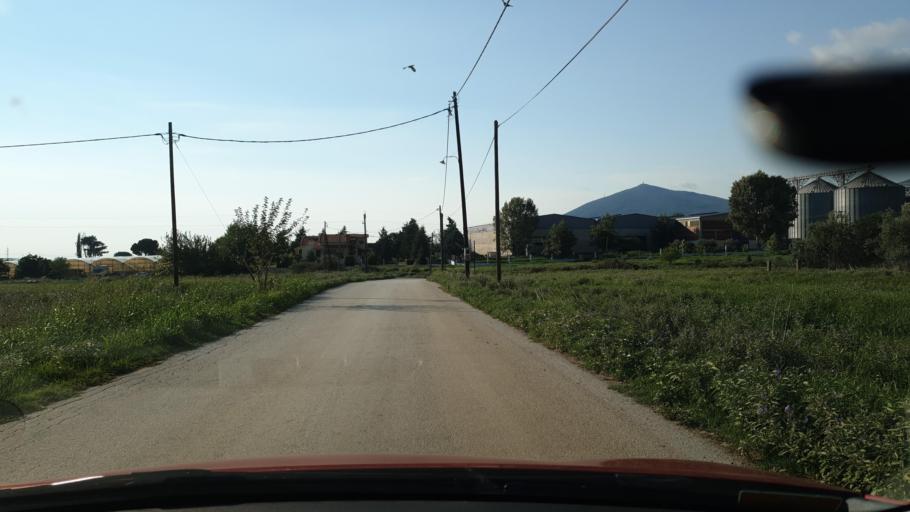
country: GR
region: Central Macedonia
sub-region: Nomos Thessalonikis
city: Vasilika
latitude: 40.4921
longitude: 23.1400
